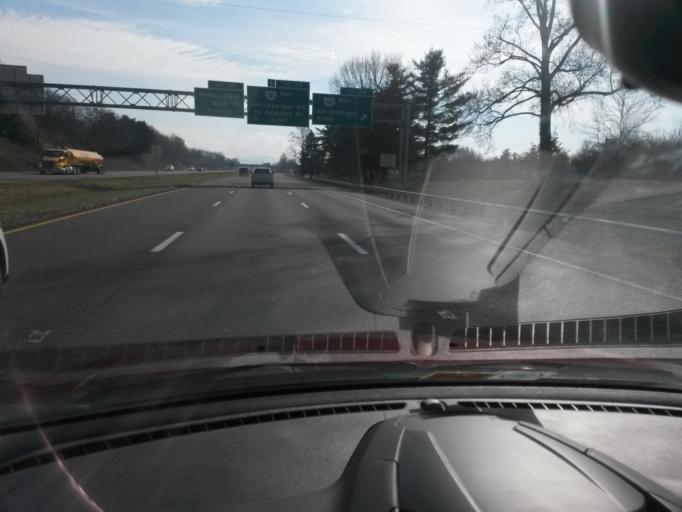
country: US
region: Virginia
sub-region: Roanoke County
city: Hollins
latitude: 37.3133
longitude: -79.9788
